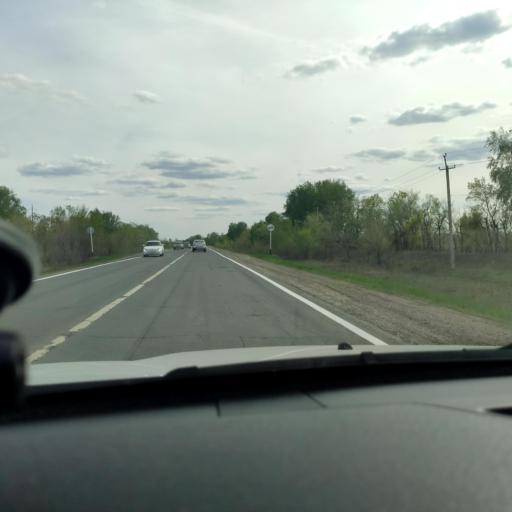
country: RU
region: Samara
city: Kinel'
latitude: 53.1757
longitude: 50.6400
